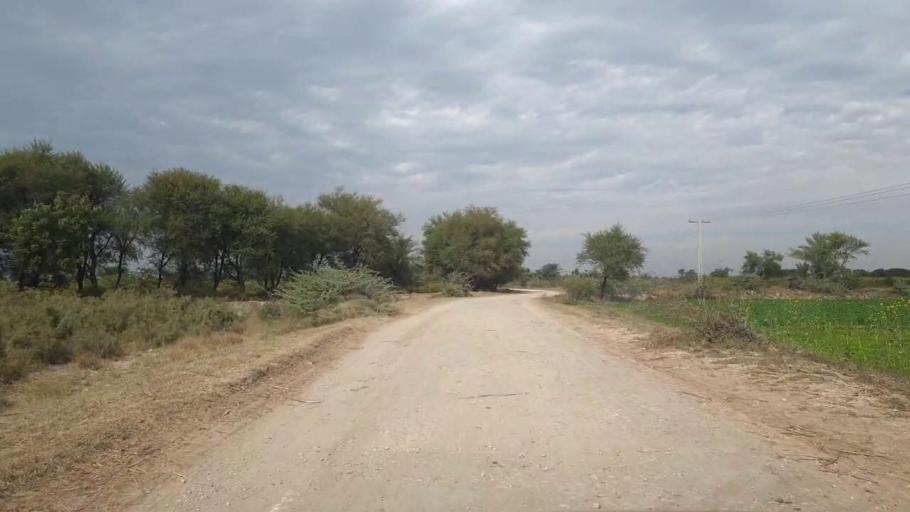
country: PK
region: Sindh
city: Sinjhoro
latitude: 26.0219
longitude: 68.8746
